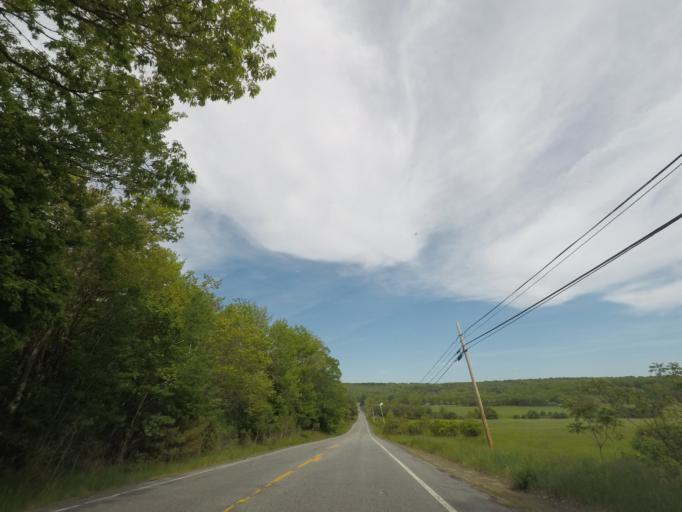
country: US
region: Maine
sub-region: Sagadahoc County
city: Richmond
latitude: 44.0857
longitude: -69.7589
